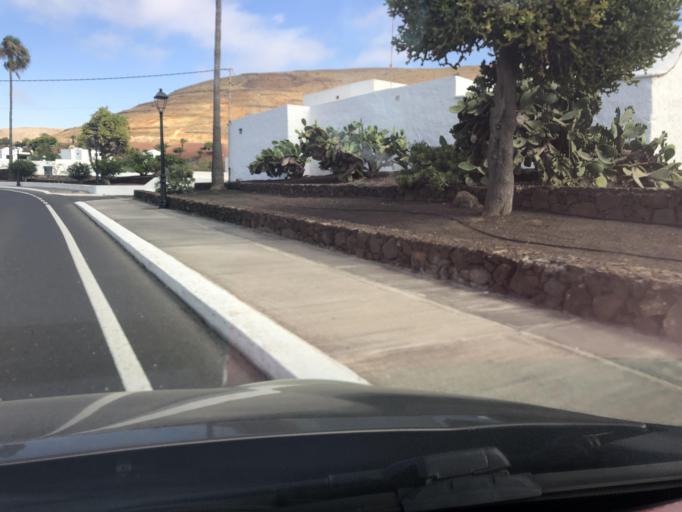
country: ES
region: Canary Islands
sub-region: Provincia de Las Palmas
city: Yaiza
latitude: 28.9530
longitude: -13.7695
